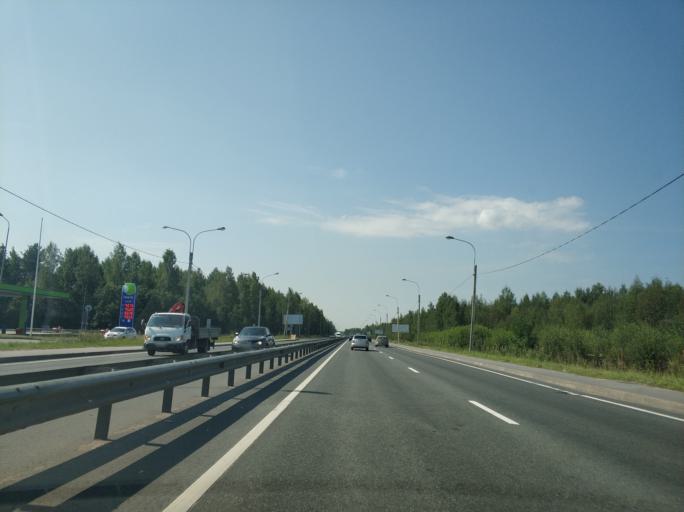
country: RU
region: Leningrad
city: Vsevolozhsk
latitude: 60.0209
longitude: 30.6019
